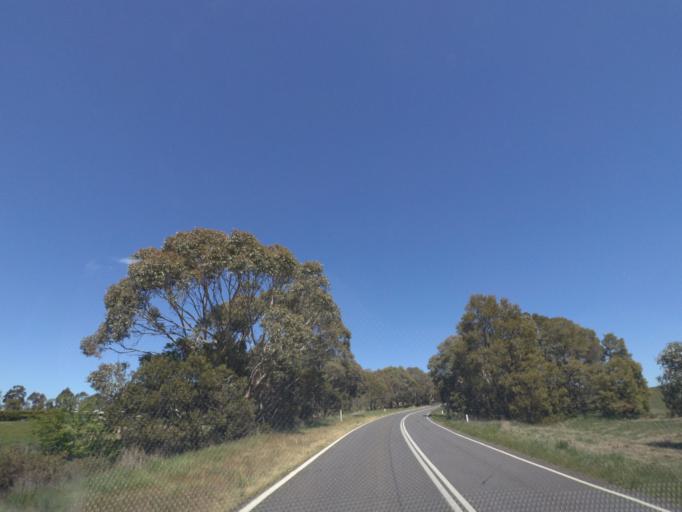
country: AU
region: Victoria
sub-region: Hume
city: Sunbury
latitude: -37.2895
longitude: 144.7039
